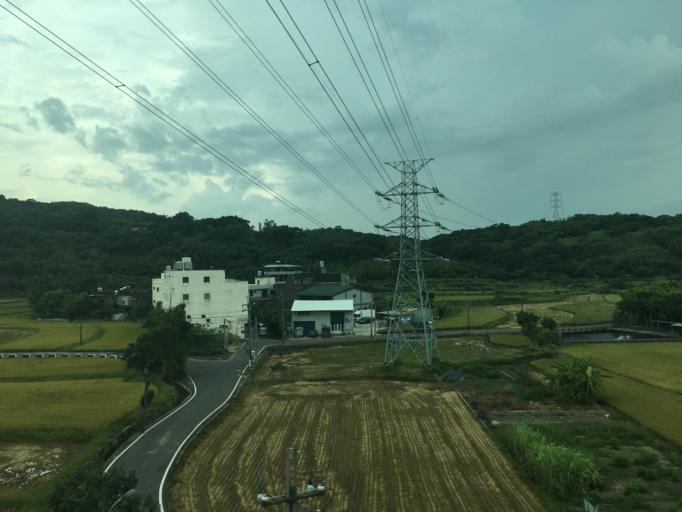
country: TW
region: Taiwan
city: Taoyuan City
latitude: 25.0807
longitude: 121.2936
